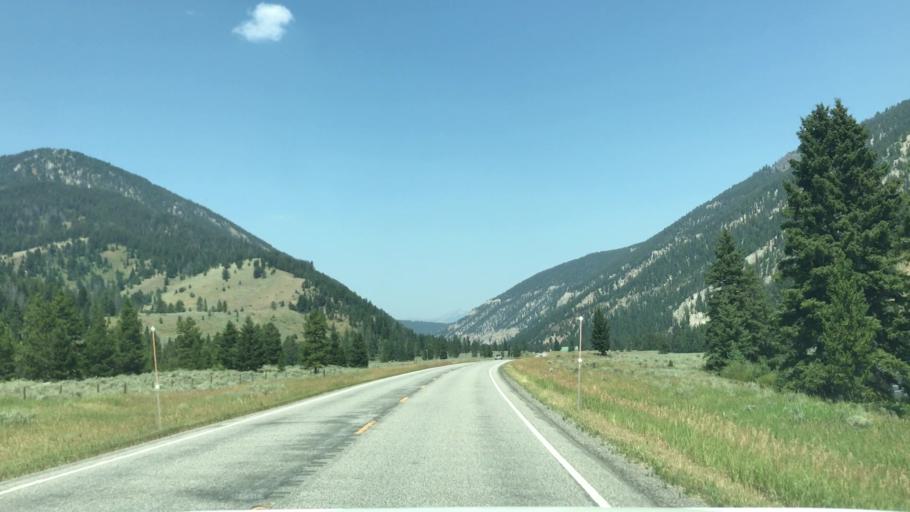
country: US
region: Montana
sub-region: Gallatin County
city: Big Sky
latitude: 45.1061
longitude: -111.2222
